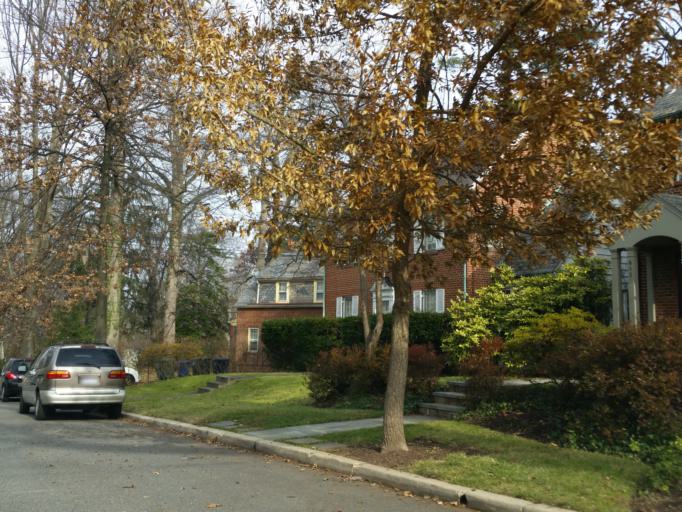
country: US
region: Maryland
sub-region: Montgomery County
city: Chevy Chase
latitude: 38.9748
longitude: -77.0664
